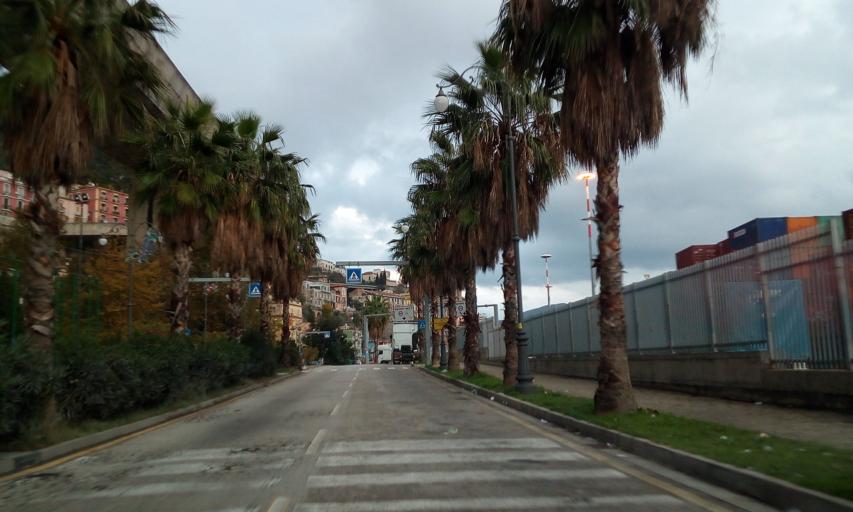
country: IT
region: Campania
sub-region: Provincia di Salerno
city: Vietri sul Mare
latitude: 40.6767
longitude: 14.7411
